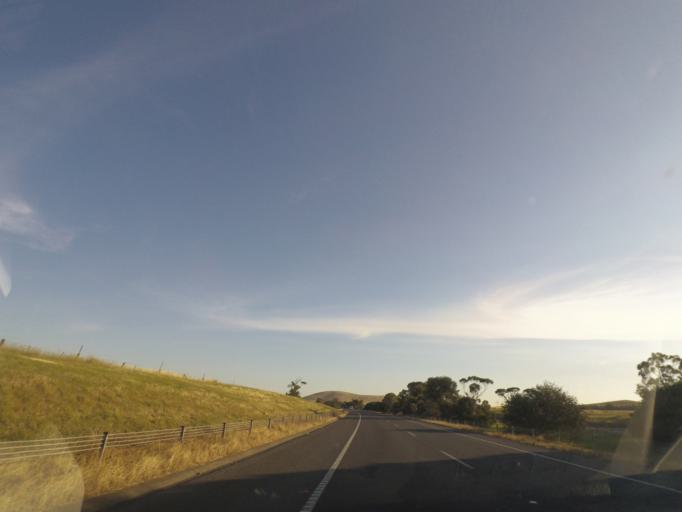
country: AU
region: Victoria
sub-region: Whittlesea
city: Whittlesea
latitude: -37.4368
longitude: 144.9817
